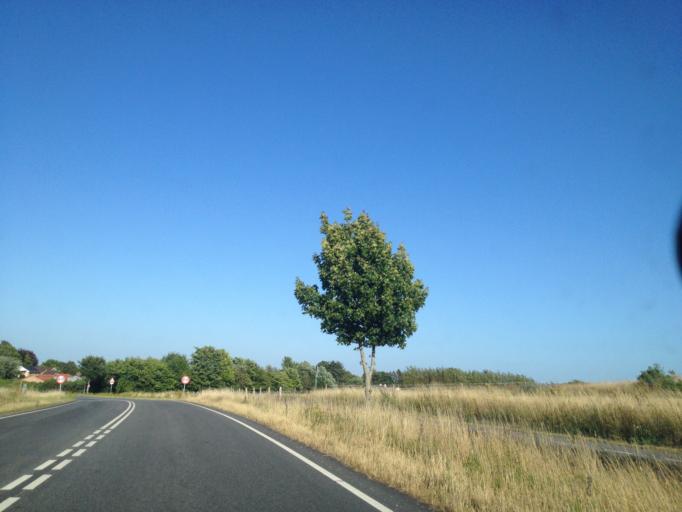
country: DK
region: Capital Region
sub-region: Gribskov Kommune
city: Helsinge
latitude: 56.0147
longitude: 12.1524
